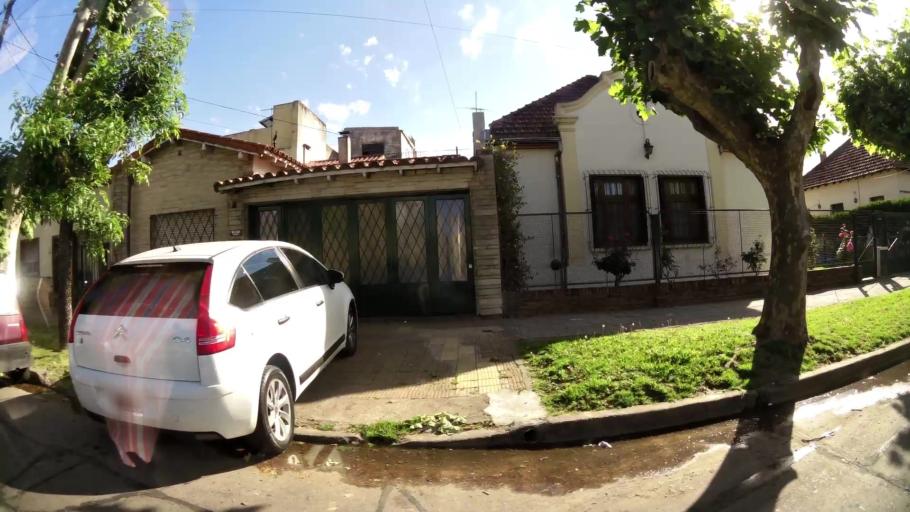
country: AR
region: Buenos Aires
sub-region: Partido de General San Martin
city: General San Martin
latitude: -34.5457
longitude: -58.5500
